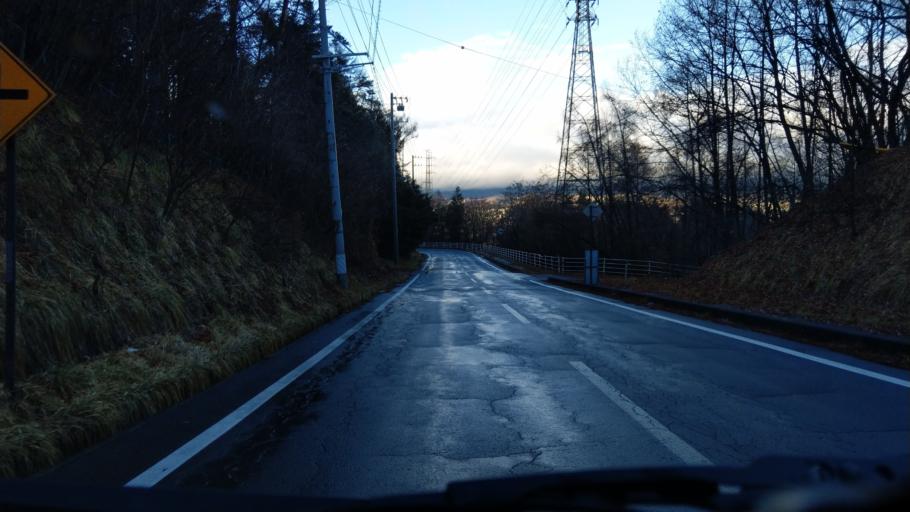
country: JP
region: Nagano
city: Komoro
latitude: 36.2959
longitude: 138.4159
